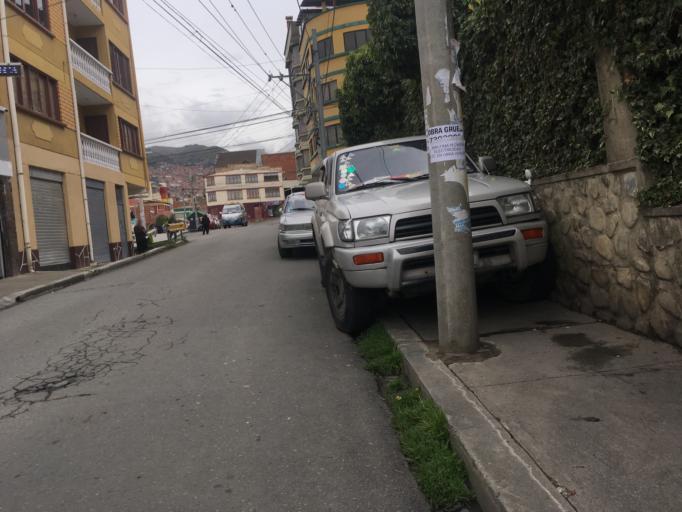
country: BO
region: La Paz
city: La Paz
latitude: -16.4916
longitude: -68.1168
